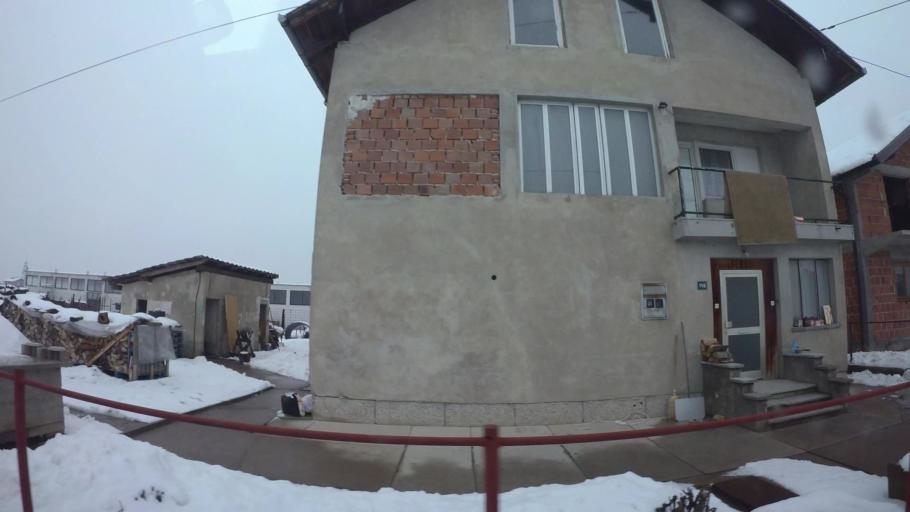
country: BA
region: Federation of Bosnia and Herzegovina
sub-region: Kanton Sarajevo
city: Sarajevo
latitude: 43.8408
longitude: 18.3099
